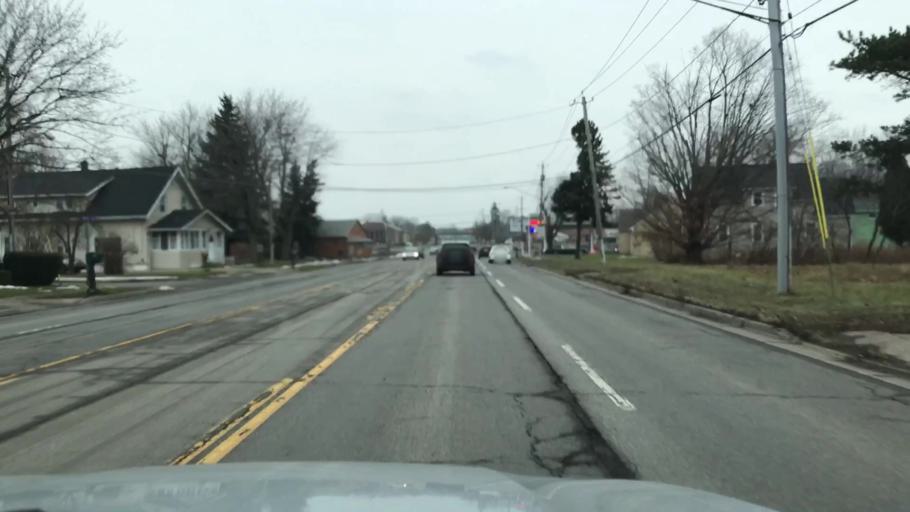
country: US
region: New York
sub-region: Erie County
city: Blasdell
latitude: 42.8072
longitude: -78.7981
